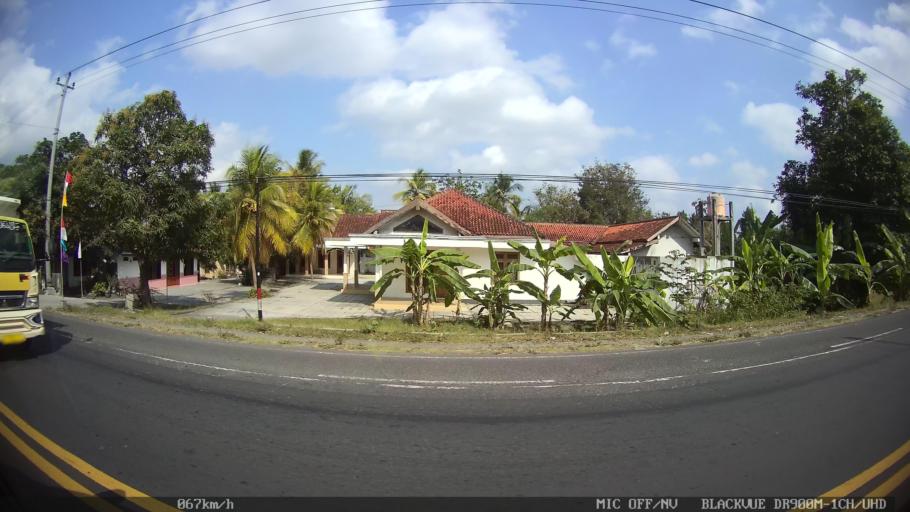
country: ID
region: Daerah Istimewa Yogyakarta
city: Srandakan
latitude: -7.8696
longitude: 110.2092
